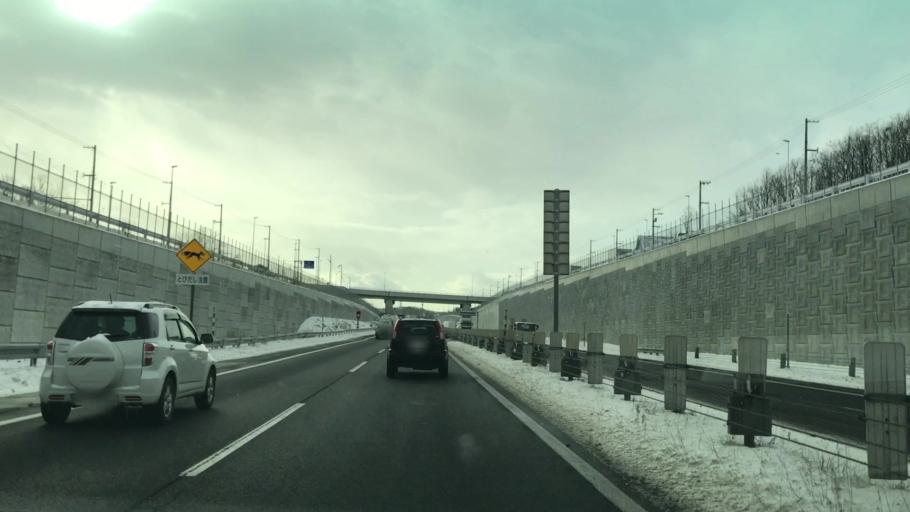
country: JP
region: Hokkaido
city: Kitahiroshima
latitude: 42.9959
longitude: 141.4688
